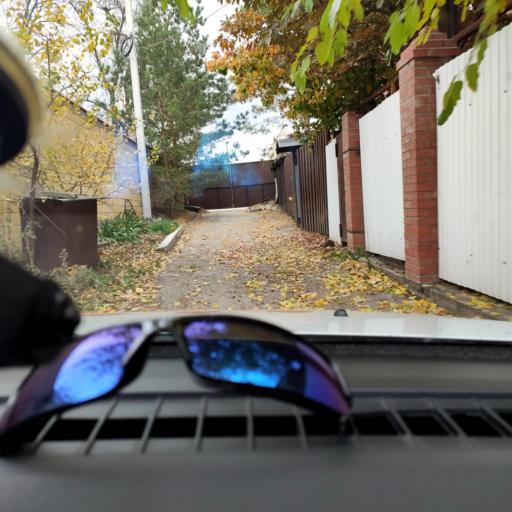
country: RU
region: Samara
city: Samara
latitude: 53.2692
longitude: 50.1945
